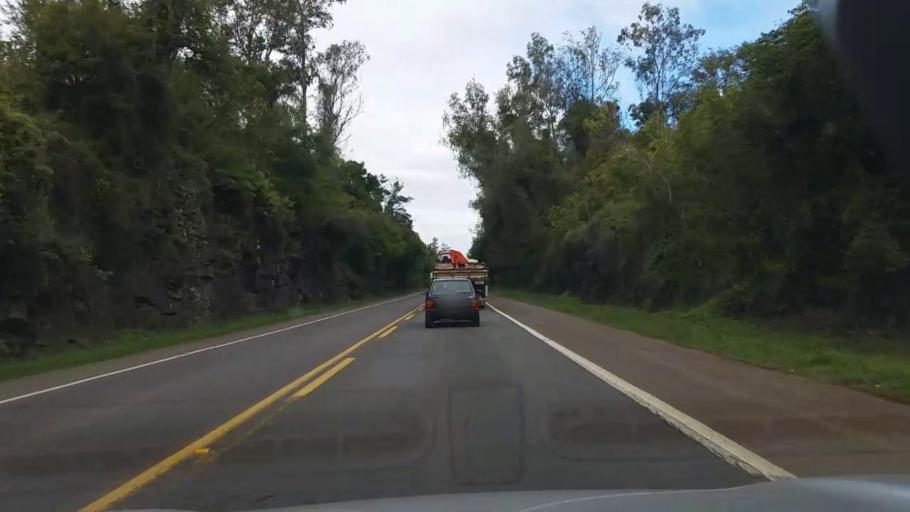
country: BR
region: Rio Grande do Sul
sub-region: Lajeado
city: Lajeado
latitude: -29.4182
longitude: -52.0239
